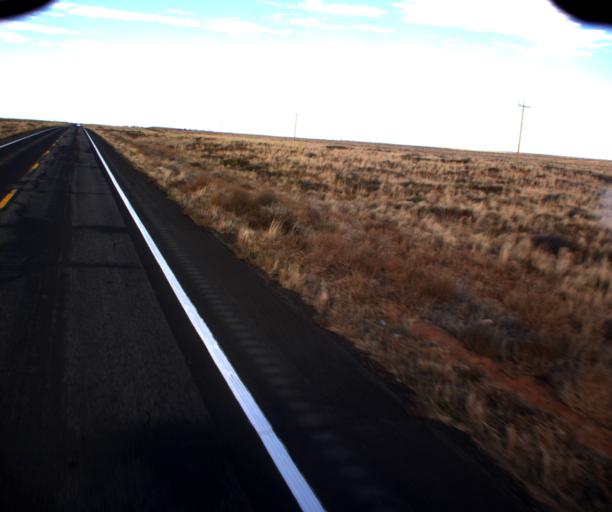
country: US
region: Arizona
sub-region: Apache County
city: Lukachukai
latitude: 36.9588
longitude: -109.3206
